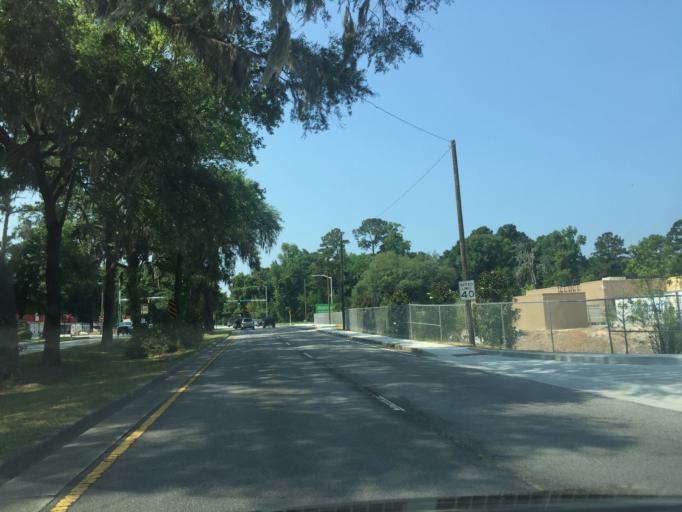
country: US
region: Georgia
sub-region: Chatham County
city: Montgomery
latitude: 31.9841
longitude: -81.1300
